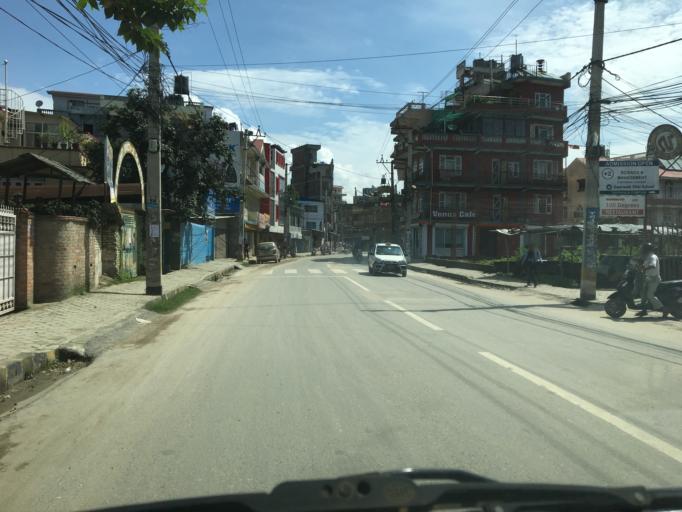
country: NP
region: Central Region
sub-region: Bagmati Zone
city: Kathmandu
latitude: 27.7129
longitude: 85.3418
